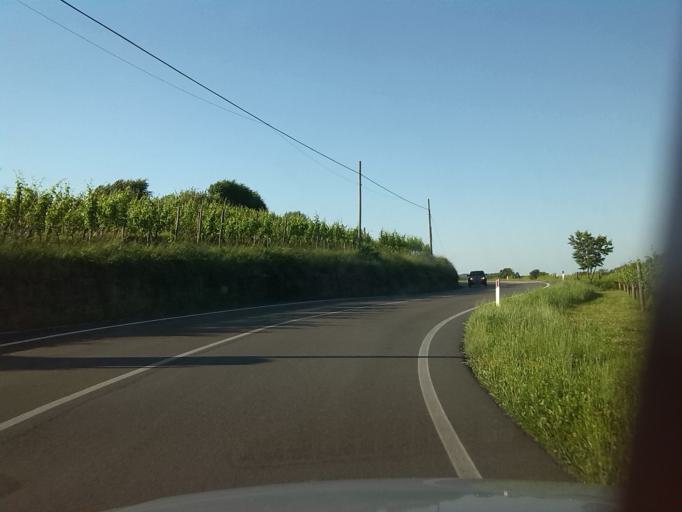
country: IT
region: Friuli Venezia Giulia
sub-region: Provincia di Udine
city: Prepotto
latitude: 46.0401
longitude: 13.4777
